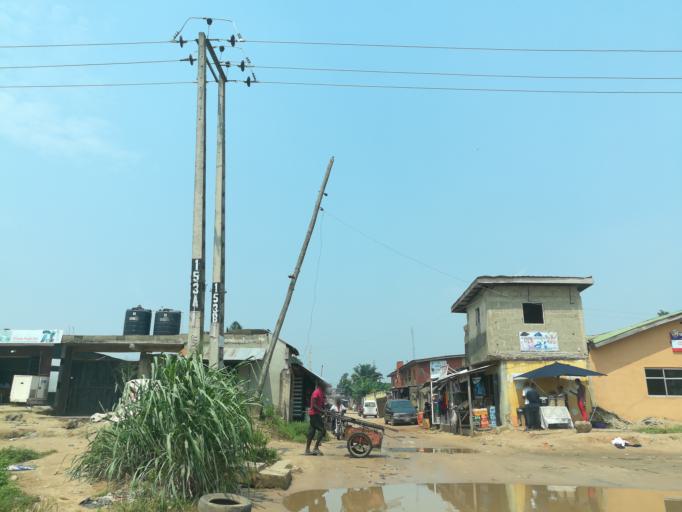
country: NG
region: Lagos
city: Ikorodu
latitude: 6.6320
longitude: 3.4830
